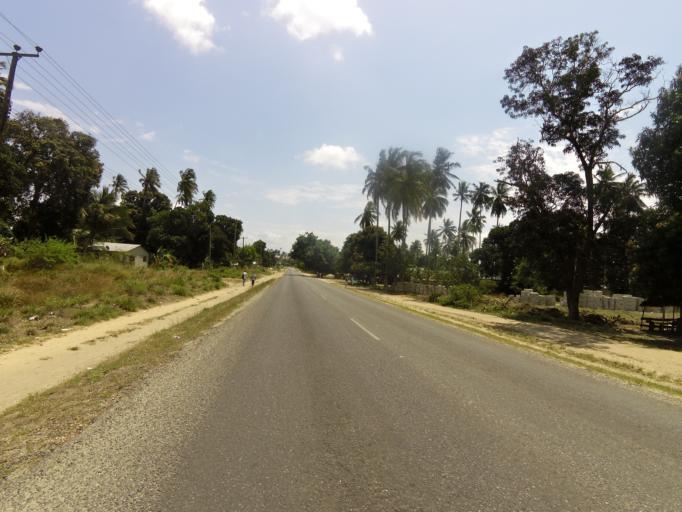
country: TZ
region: Pwani
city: Vikindu
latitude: -7.0332
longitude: 39.2782
